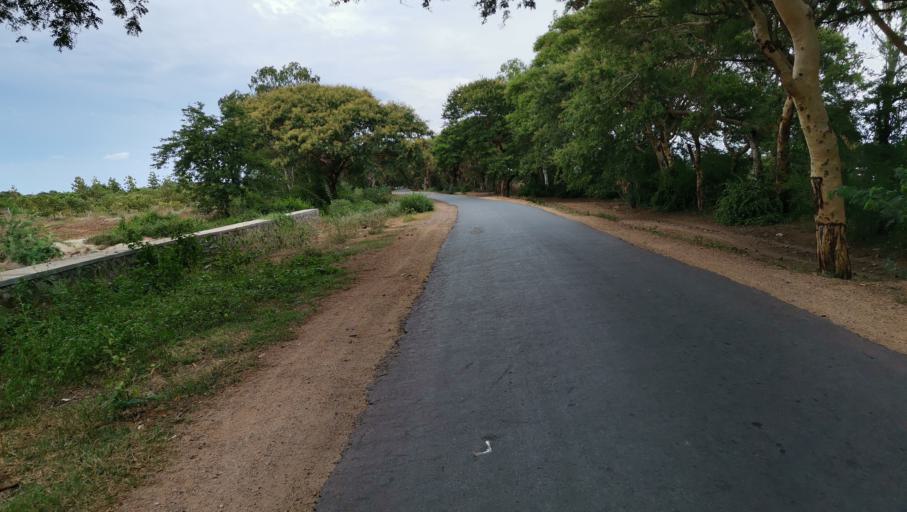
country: MM
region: Sagain
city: Monywa
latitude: 21.8527
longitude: 95.4368
